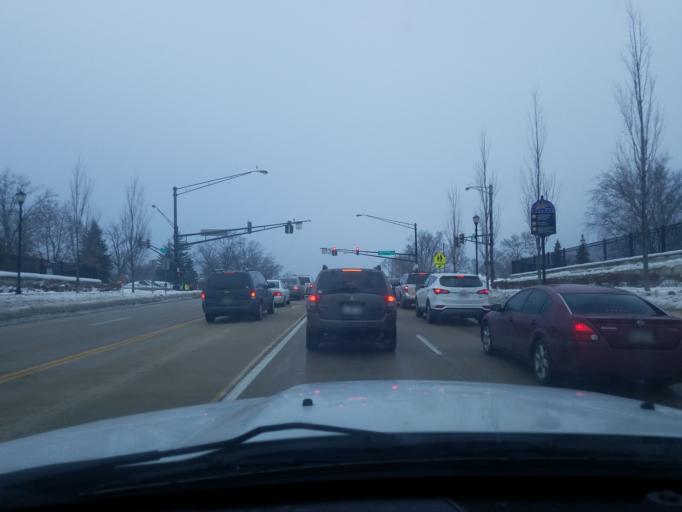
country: US
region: Indiana
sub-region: Saint Joseph County
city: Mishawaka
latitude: 41.6726
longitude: -86.1810
